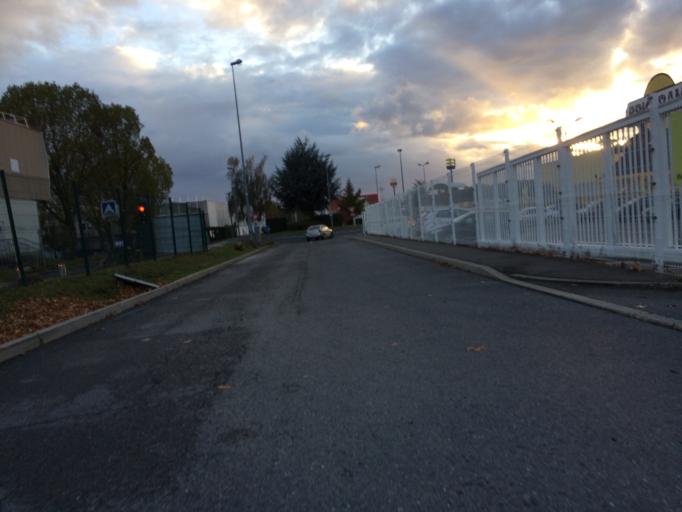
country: FR
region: Ile-de-France
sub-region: Departement de l'Essonne
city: Orsay
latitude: 48.6847
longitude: 2.2079
